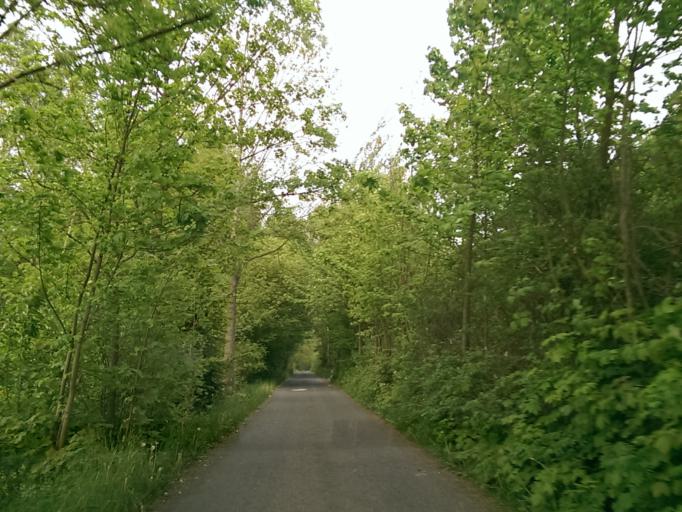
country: CZ
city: Plavy
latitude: 50.7008
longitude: 15.3124
